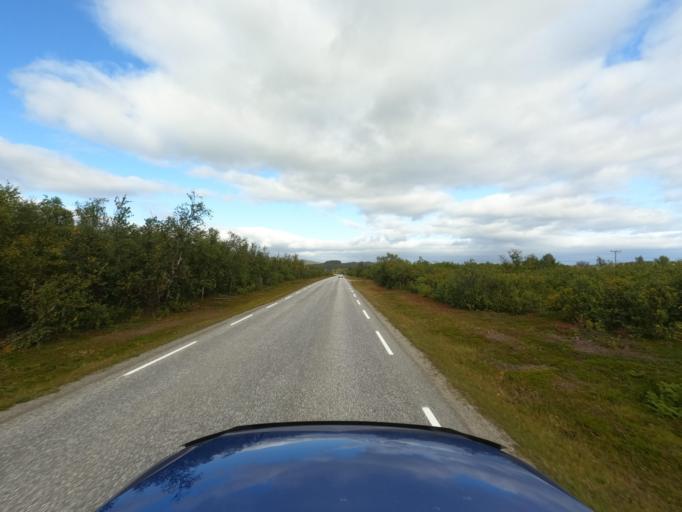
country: NO
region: Finnmark Fylke
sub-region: Porsanger
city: Lakselv
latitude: 70.1898
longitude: 24.9148
